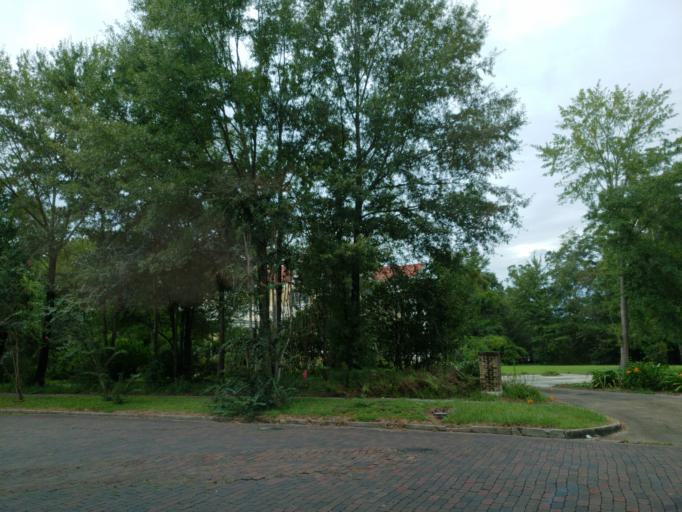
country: US
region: Mississippi
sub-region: Forrest County
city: Hattiesburg
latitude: 31.3228
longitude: -89.3040
